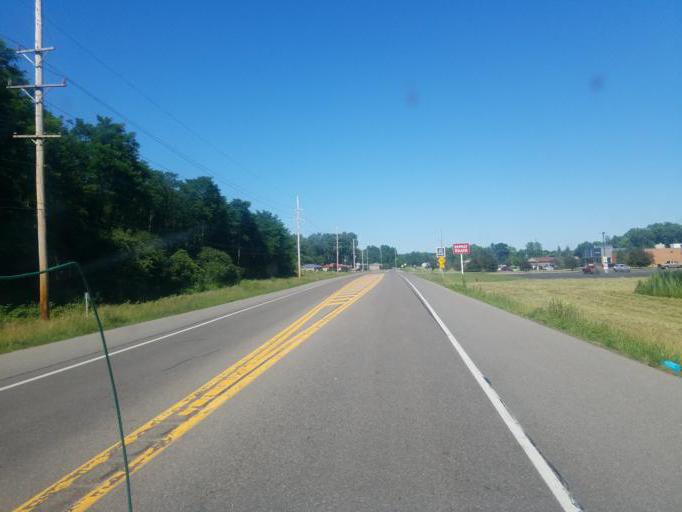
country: US
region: New York
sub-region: Wayne County
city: Lyons
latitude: 43.0595
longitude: -77.0048
